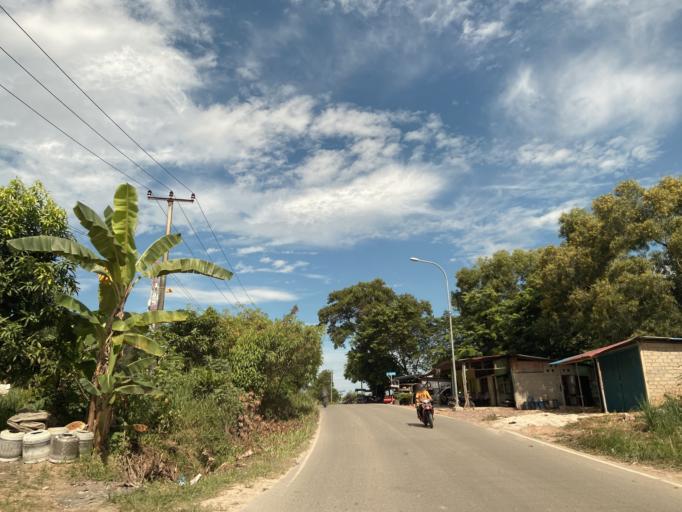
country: SG
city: Singapore
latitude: 1.0334
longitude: 103.9397
